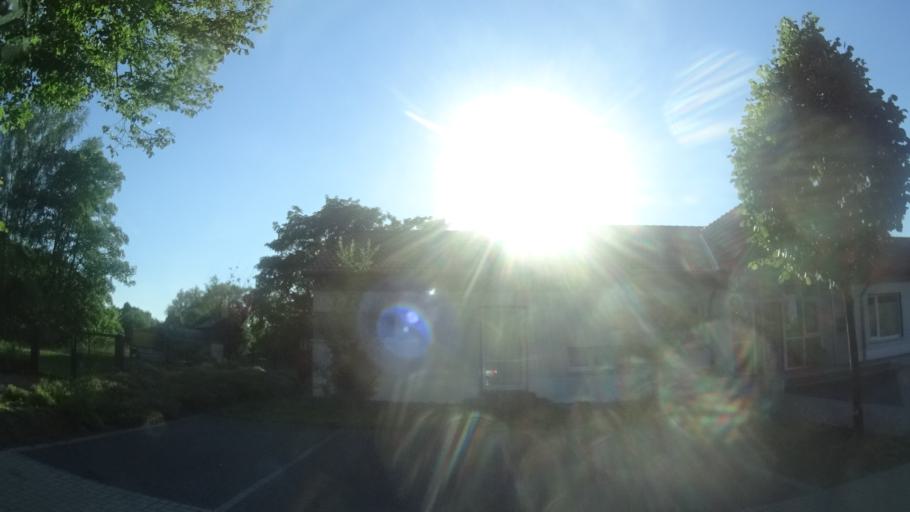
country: DE
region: Lower Saxony
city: Baddeckenstedt
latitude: 52.0860
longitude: 10.2326
